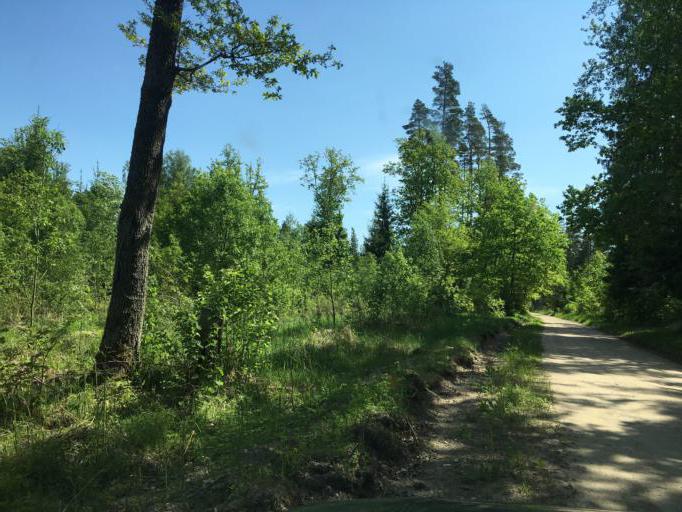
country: LV
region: Talsu Rajons
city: Valdemarpils
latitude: 57.3678
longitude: 22.6224
